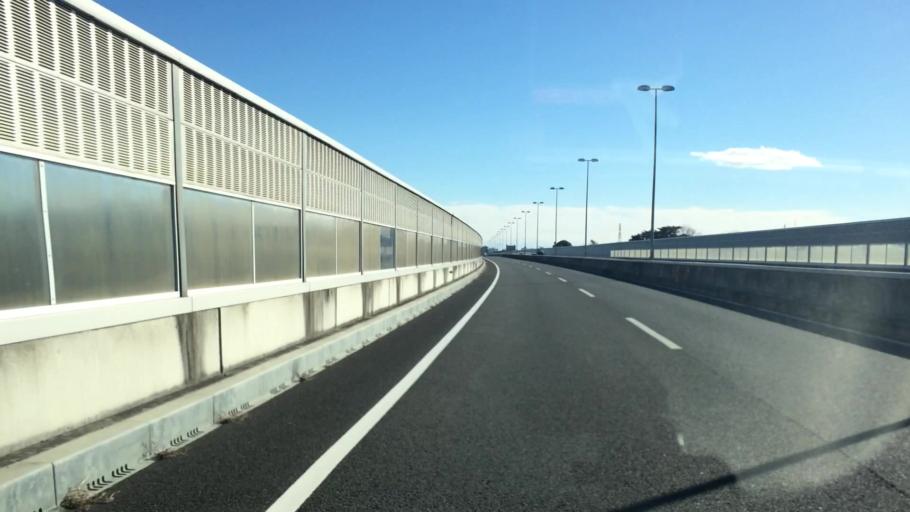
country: JP
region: Tochigi
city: Utsunomiya-shi
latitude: 36.6051
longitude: 139.8600
